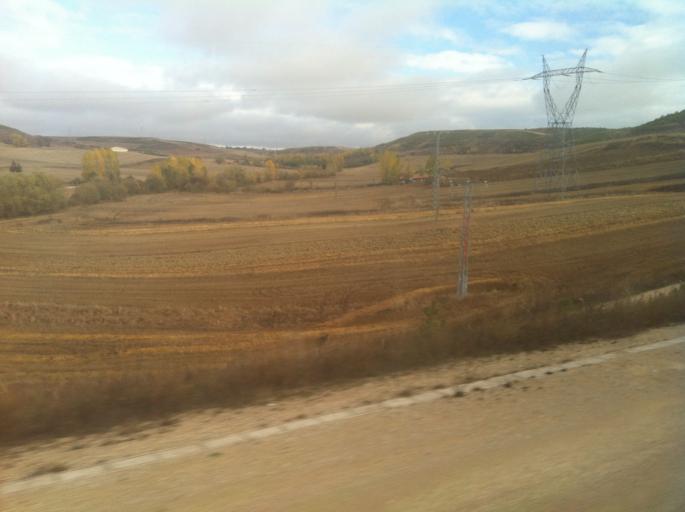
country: ES
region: Castille and Leon
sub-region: Provincia de Burgos
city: Hurones
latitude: 42.3753
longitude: -3.6094
